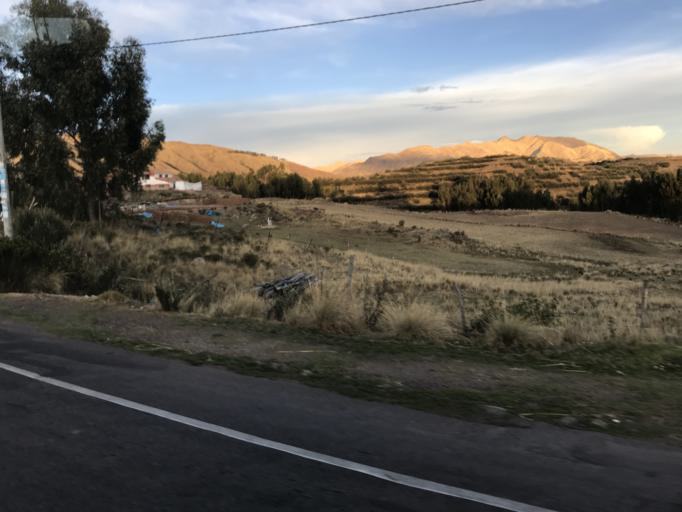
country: PE
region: Cusco
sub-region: Provincia de Cusco
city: Cusco
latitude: -13.4928
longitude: -71.9673
